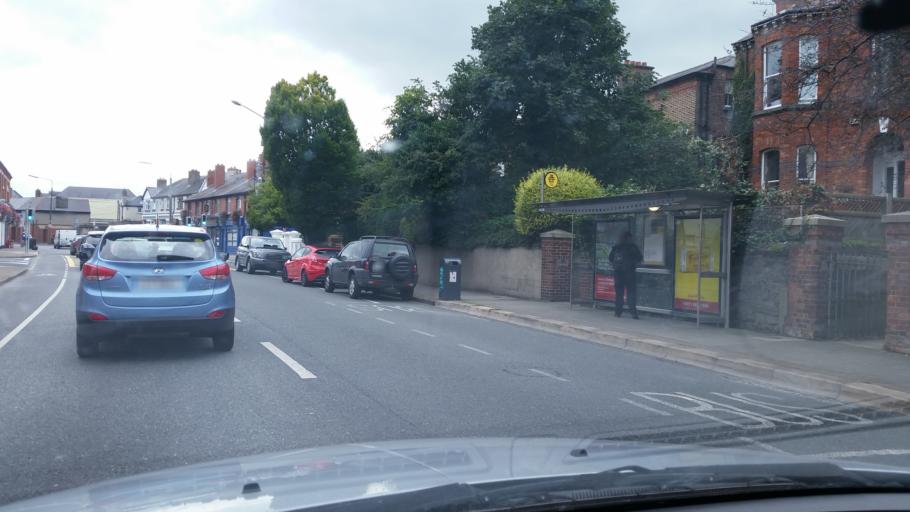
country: IE
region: Leinster
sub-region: South Dublin
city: Terenure
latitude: 53.3151
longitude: -6.2820
